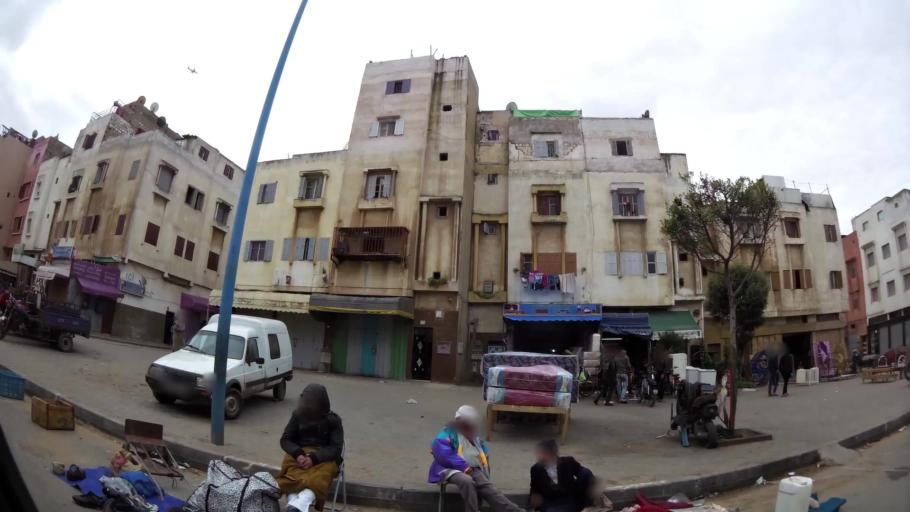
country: MA
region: Grand Casablanca
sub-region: Mediouna
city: Tit Mellil
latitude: 33.5620
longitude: -7.5438
